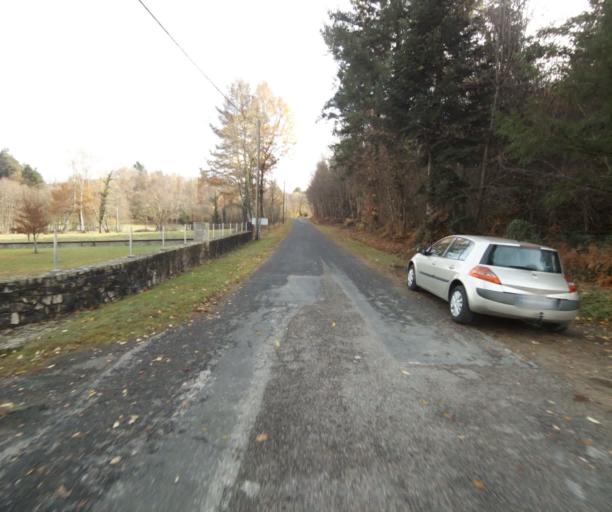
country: FR
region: Limousin
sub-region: Departement de la Correze
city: Sainte-Fortunade
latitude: 45.1948
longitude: 1.7363
